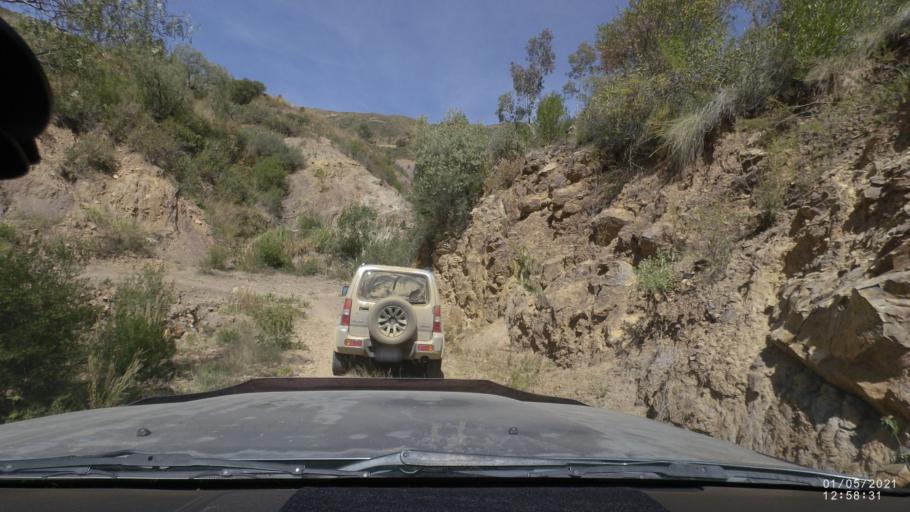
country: BO
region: Cochabamba
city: Capinota
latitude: -17.6844
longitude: -66.1657
